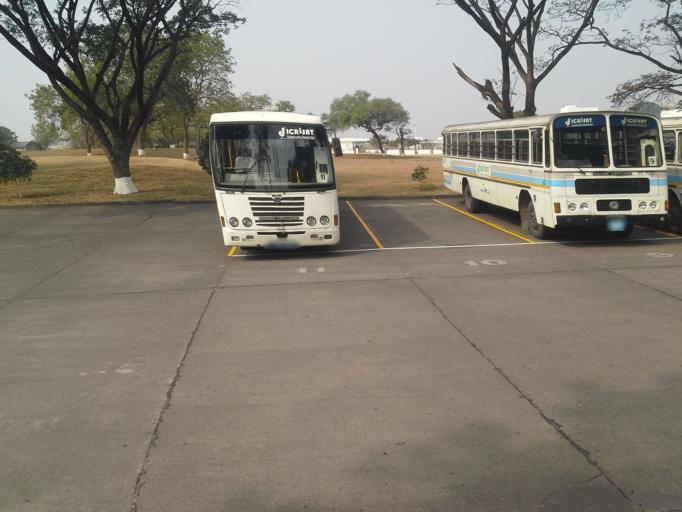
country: IN
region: Telangana
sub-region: Medak
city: Patancheru
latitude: 17.5126
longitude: 78.2735
